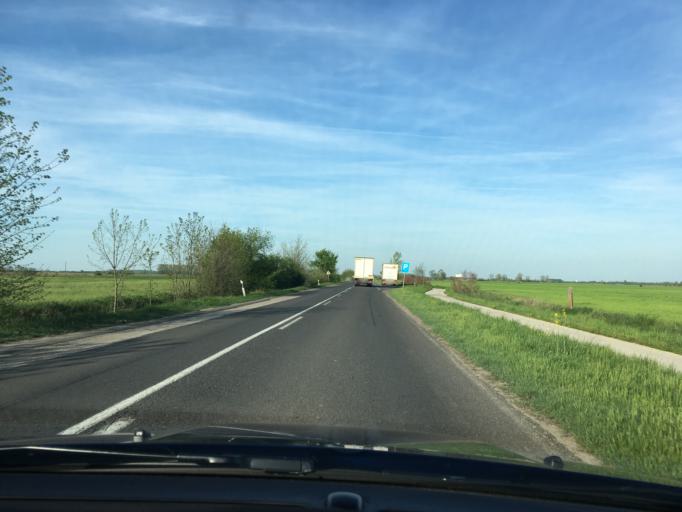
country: HU
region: Bekes
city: Korosladany
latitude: 46.9951
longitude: 21.0933
